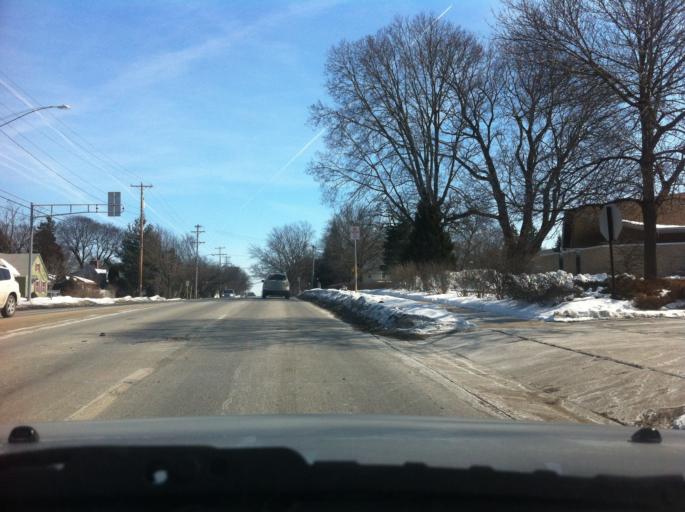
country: US
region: Wisconsin
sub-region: Dane County
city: Shorewood Hills
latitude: 43.0608
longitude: -89.4511
